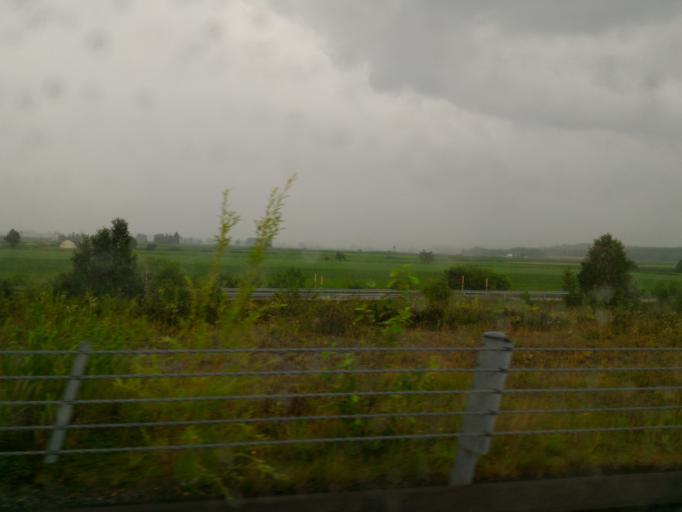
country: JP
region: Hokkaido
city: Nayoro
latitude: 44.4433
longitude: 142.3709
